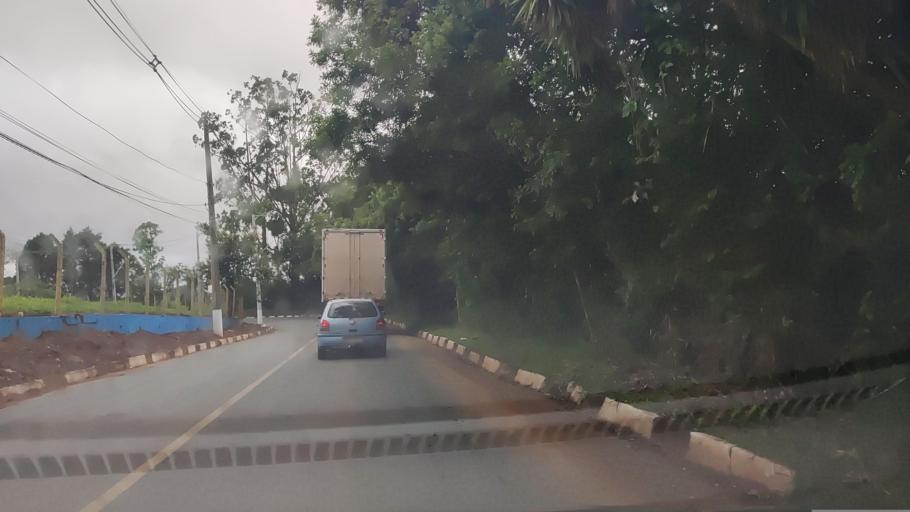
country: BR
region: Sao Paulo
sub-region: Vargem Grande Paulista
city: Vargem Grande Paulista
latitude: -23.6498
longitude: -47.0516
